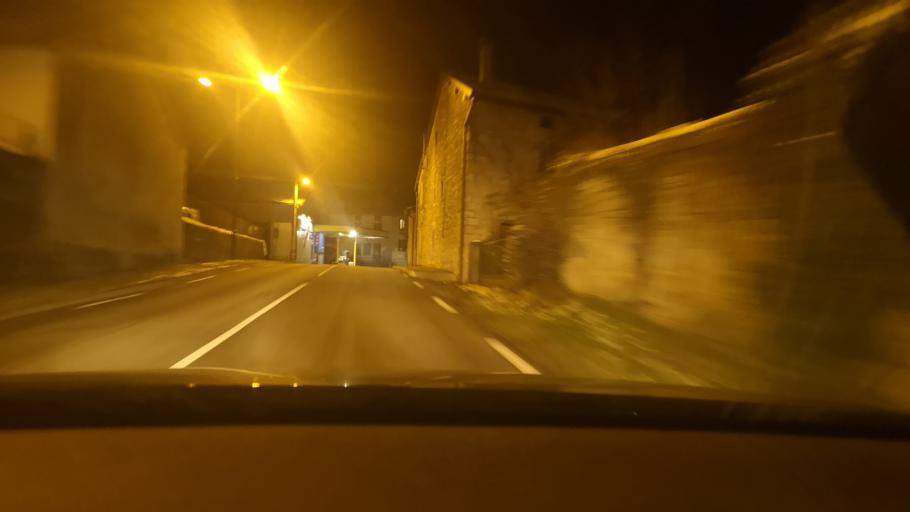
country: FR
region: Rhone-Alpes
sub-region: Departement de l'Ain
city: Villereversure
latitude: 46.1601
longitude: 5.3883
